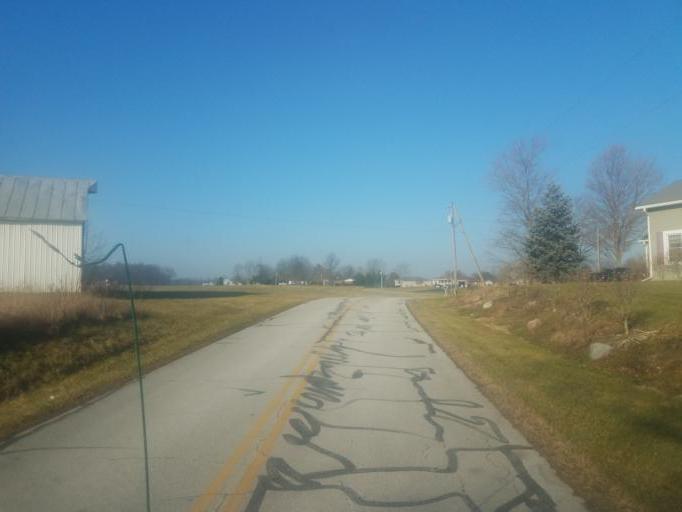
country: US
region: Ohio
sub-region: Seneca County
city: Tiffin
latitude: 41.0438
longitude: -83.0093
